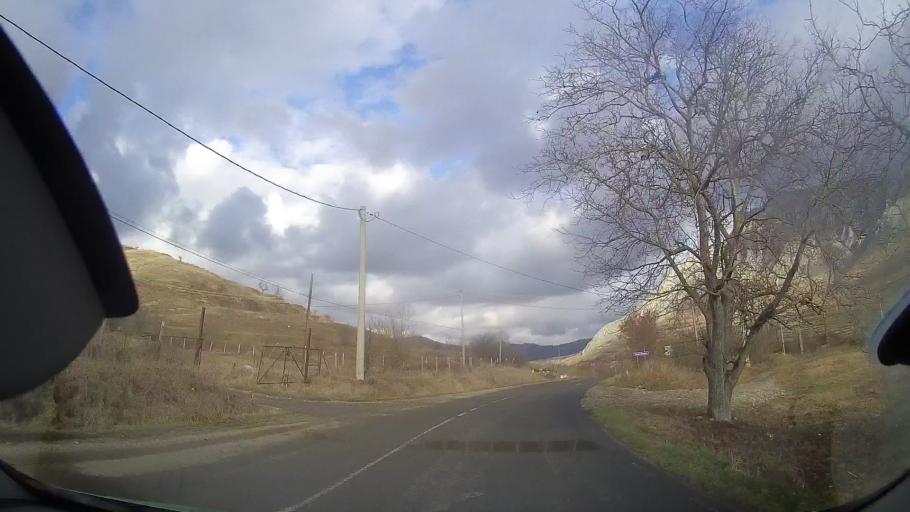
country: RO
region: Alba
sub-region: Comuna Rimetea
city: Rimetea
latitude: 46.4446
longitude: 23.5642
